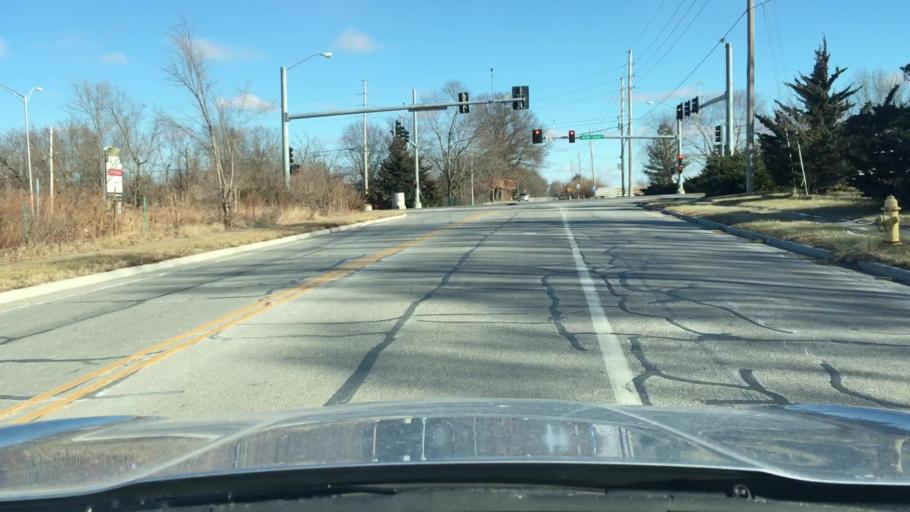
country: US
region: Missouri
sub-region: Jackson County
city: Lees Summit
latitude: 38.8897
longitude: -94.3974
